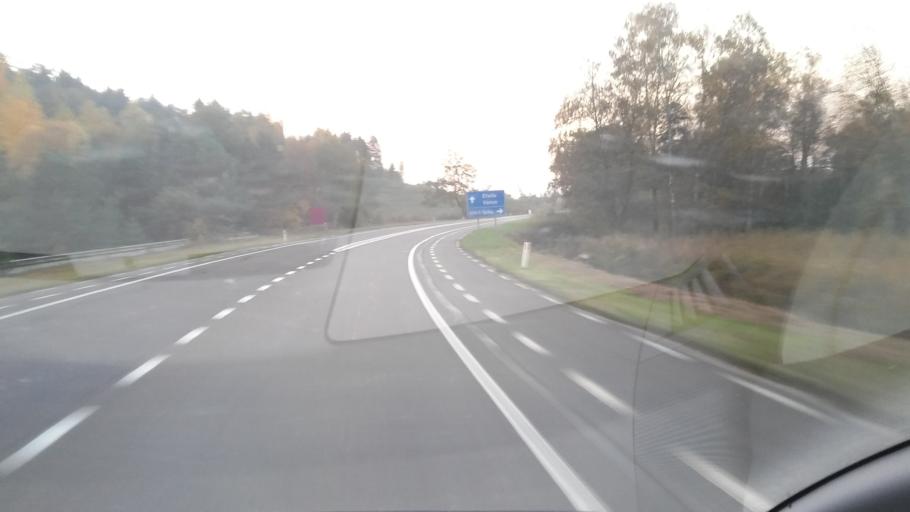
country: BE
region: Wallonia
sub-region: Province du Luxembourg
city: Saint-Leger
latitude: 49.6722
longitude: 5.6908
